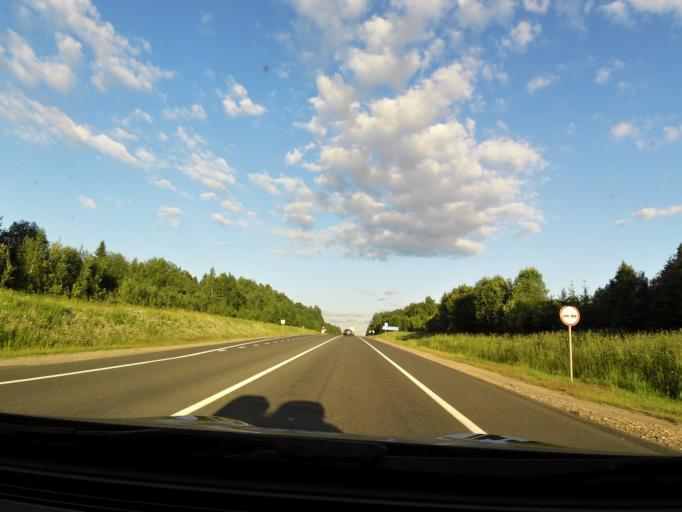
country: RU
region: Vologda
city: Gryazovets
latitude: 59.0512
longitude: 40.0820
